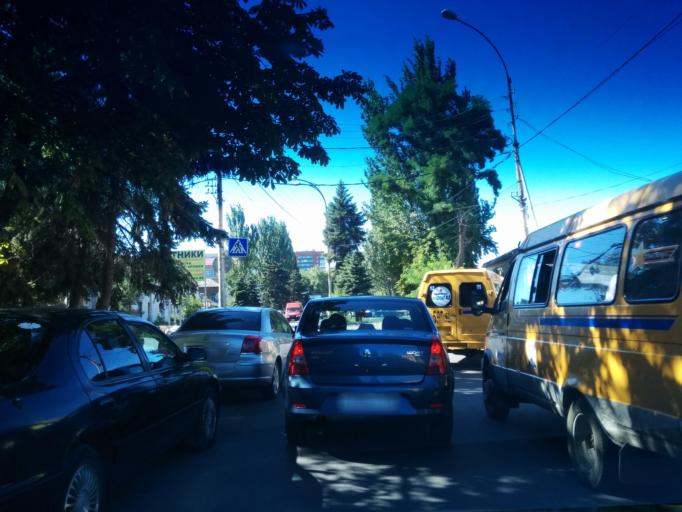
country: RU
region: Rostov
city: Shakhty
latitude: 47.7091
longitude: 40.2201
